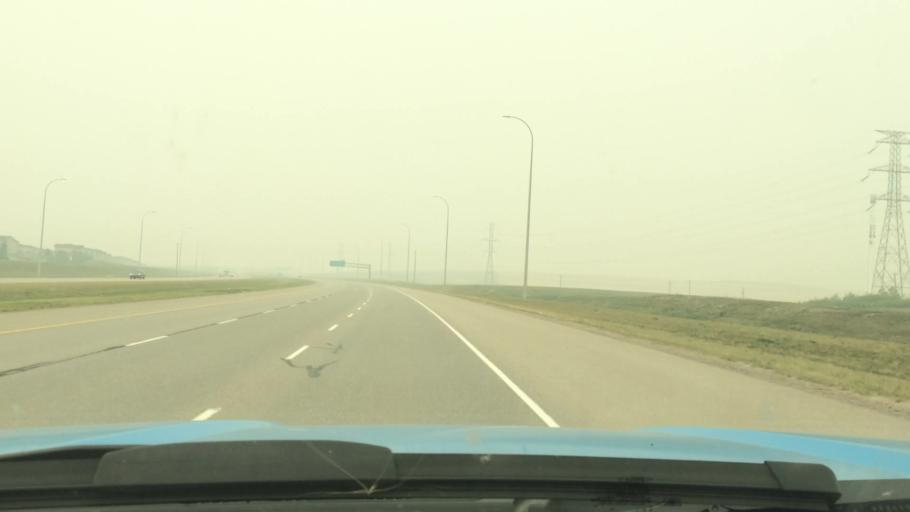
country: CA
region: Alberta
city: Airdrie
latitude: 51.1758
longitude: -114.0425
